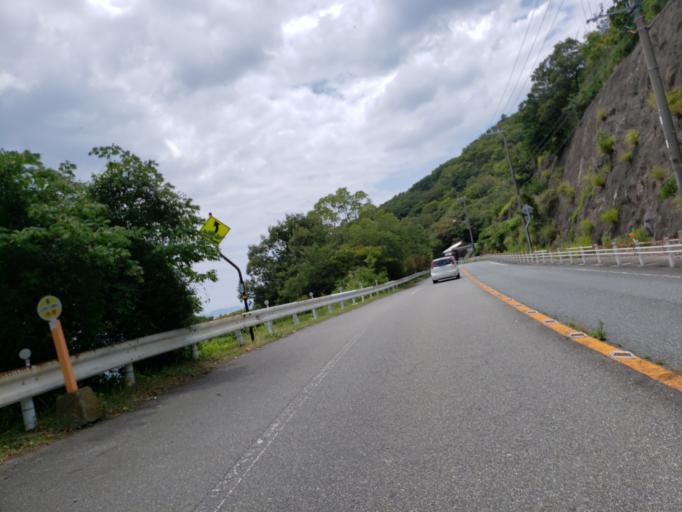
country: JP
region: Hyogo
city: Aioi
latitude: 34.7754
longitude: 134.5198
